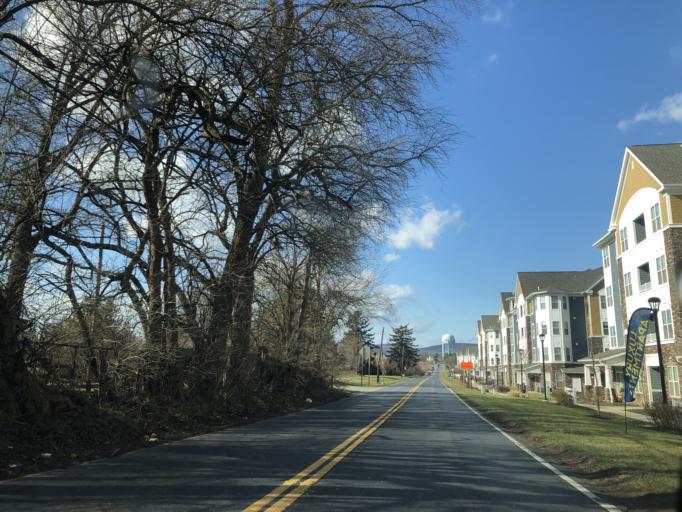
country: US
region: Maryland
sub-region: Frederick County
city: Ballenger Creek
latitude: 39.4037
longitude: -77.4419
